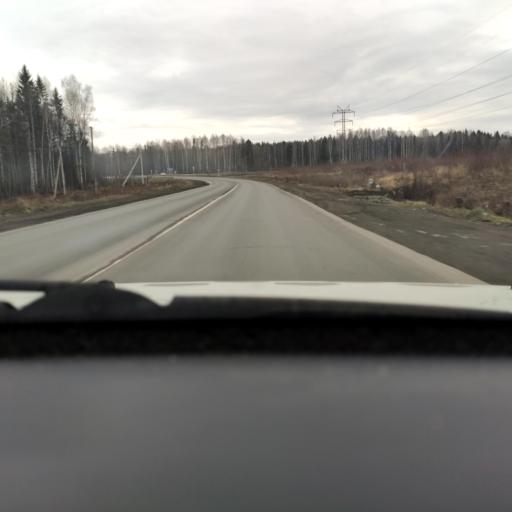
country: RU
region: Perm
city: Polazna
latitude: 58.1364
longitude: 56.4159
